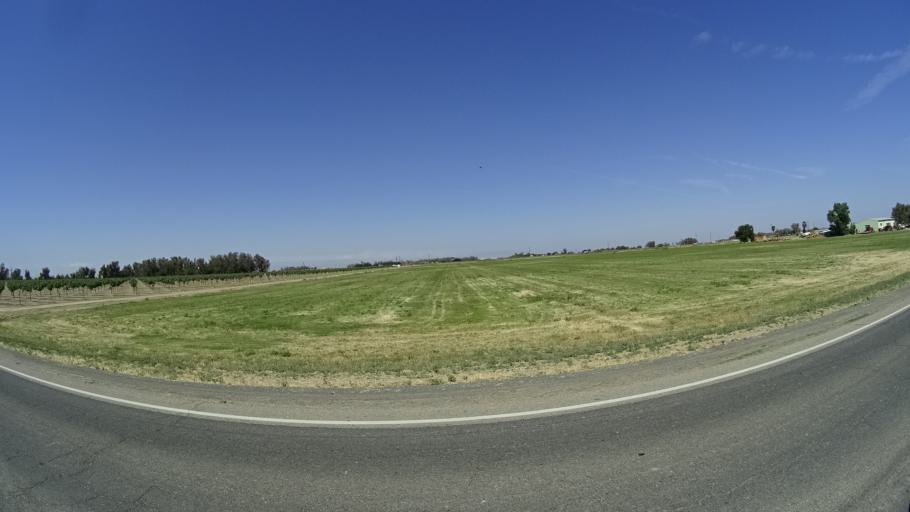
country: US
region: California
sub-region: Kings County
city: Lemoore
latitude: 36.2478
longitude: -119.7806
